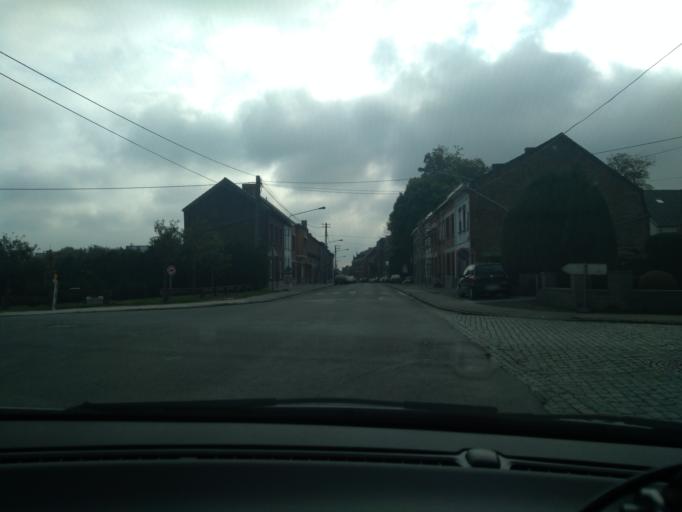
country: BE
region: Wallonia
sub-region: Province du Hainaut
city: Frameries
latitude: 50.4147
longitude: 3.8898
